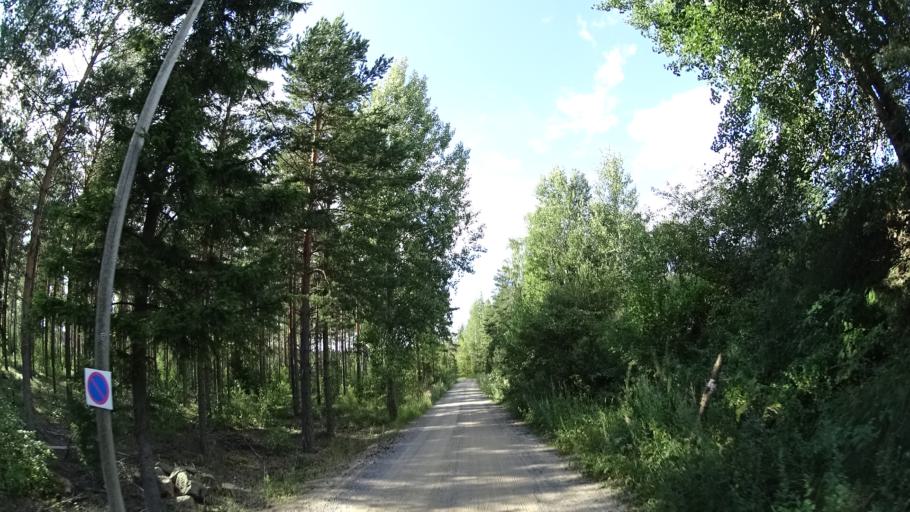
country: FI
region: Uusimaa
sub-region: Helsinki
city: Vihti
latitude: 60.3647
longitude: 24.3515
